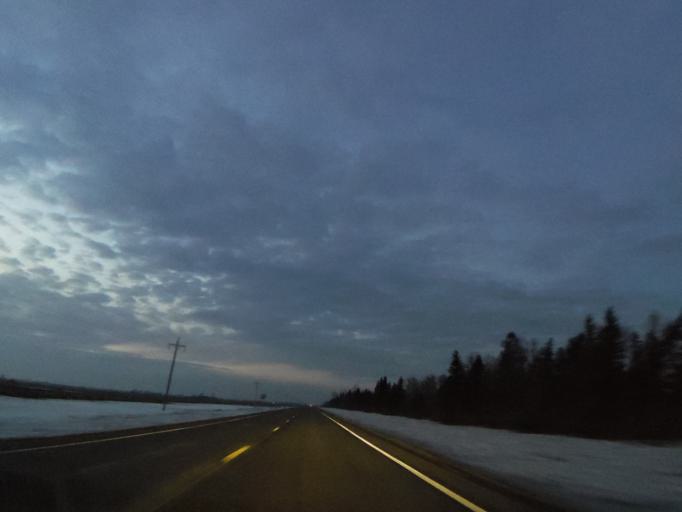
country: US
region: North Dakota
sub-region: Walsh County
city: Park River
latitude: 48.2310
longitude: -97.6226
